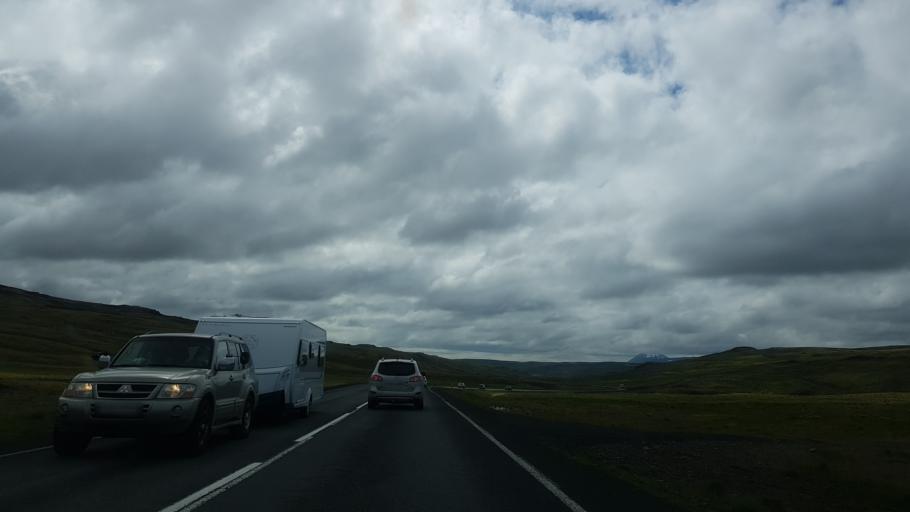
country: IS
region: West
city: Borgarnes
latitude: 64.9268
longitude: -21.1041
